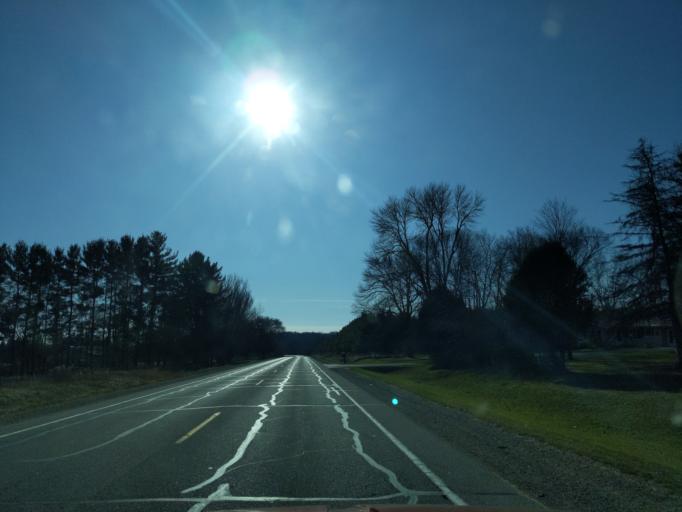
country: US
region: Wisconsin
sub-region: Waushara County
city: Wautoma
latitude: 44.0983
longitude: -89.2903
